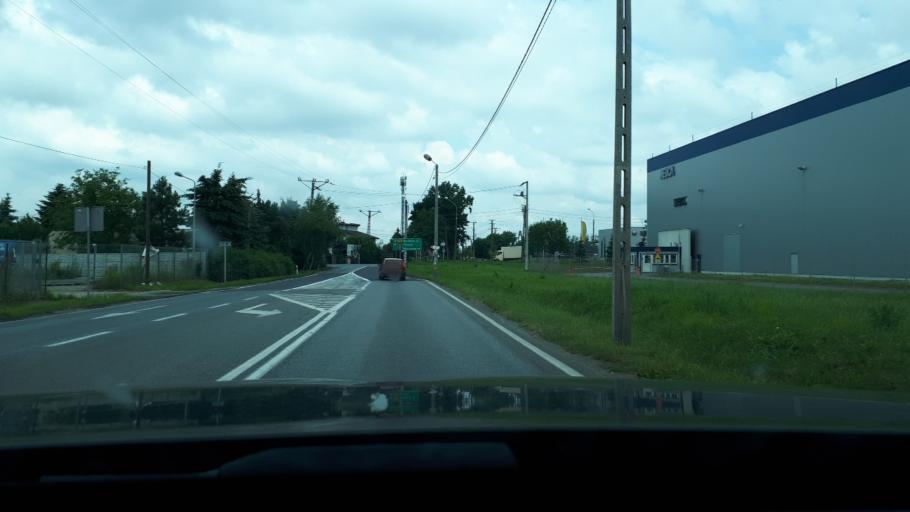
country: PL
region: Masovian Voivodeship
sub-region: Powiat warszawski zachodni
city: Ozarow Mazowiecki
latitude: 52.2100
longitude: 20.7698
